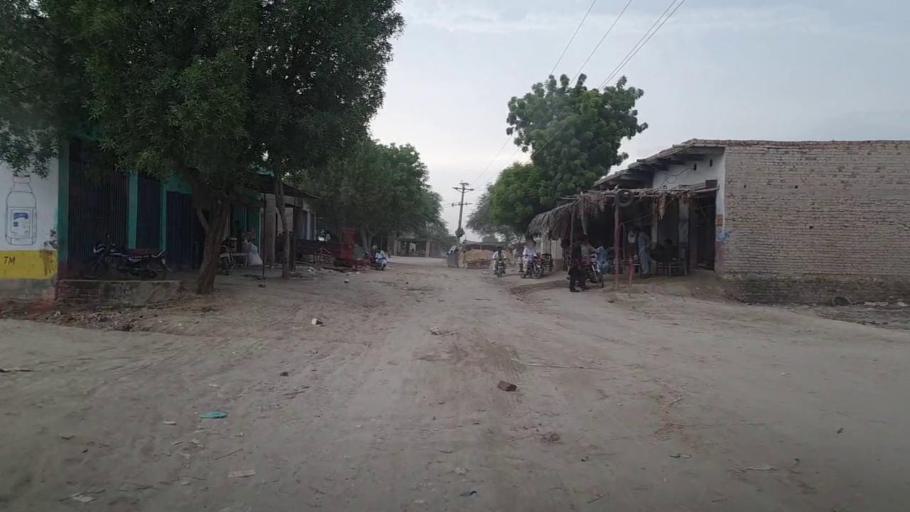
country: PK
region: Sindh
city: Karaundi
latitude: 26.9864
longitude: 68.3438
